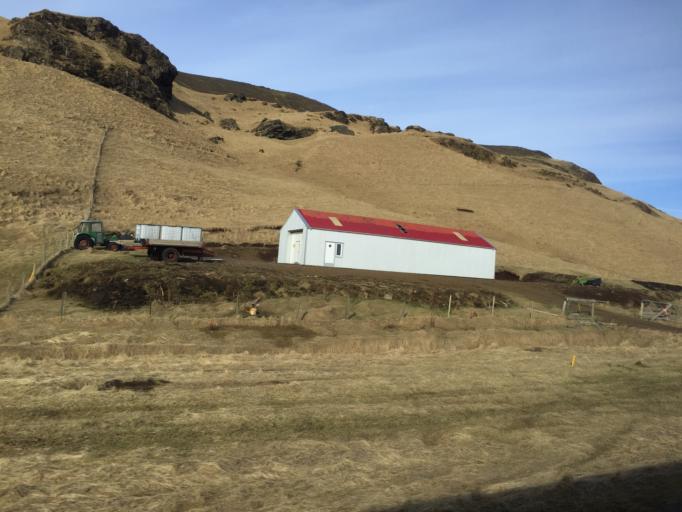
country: IS
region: South
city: Vestmannaeyjar
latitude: 63.4475
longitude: -19.1184
